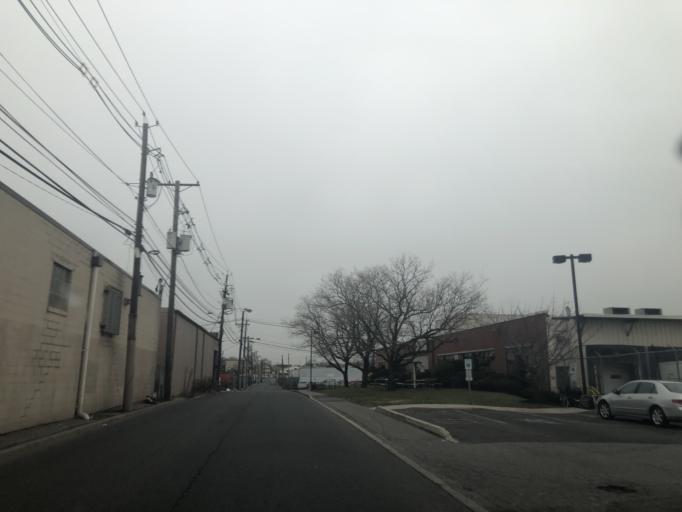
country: US
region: New Jersey
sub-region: Union County
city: Elizabeth
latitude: 40.6729
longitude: -74.1939
